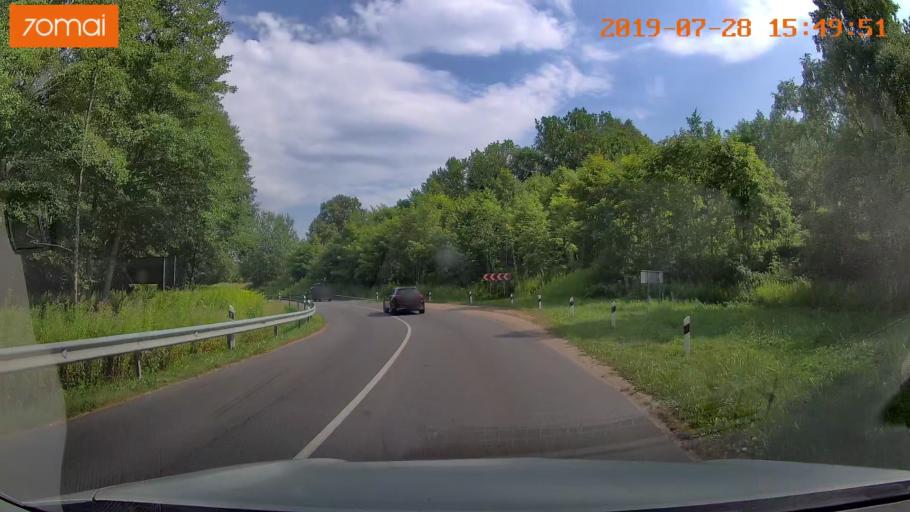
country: RU
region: Kaliningrad
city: Otradnoye
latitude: 54.9403
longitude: 20.0833
